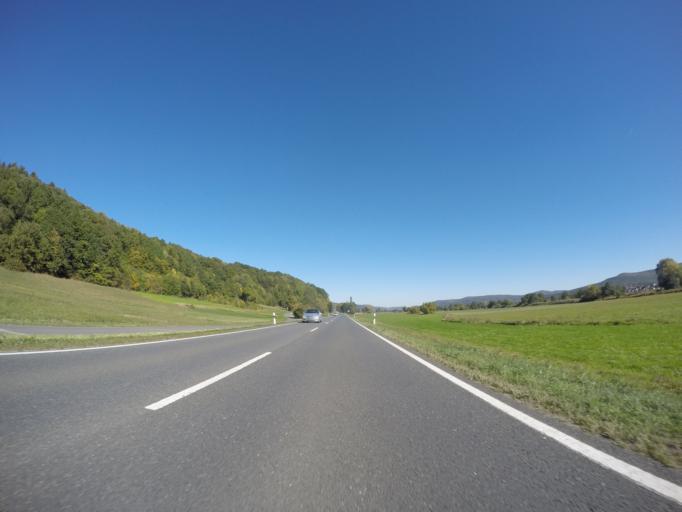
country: DE
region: Bavaria
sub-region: Upper Franconia
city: Wiesenthau
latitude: 49.7315
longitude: 11.1274
